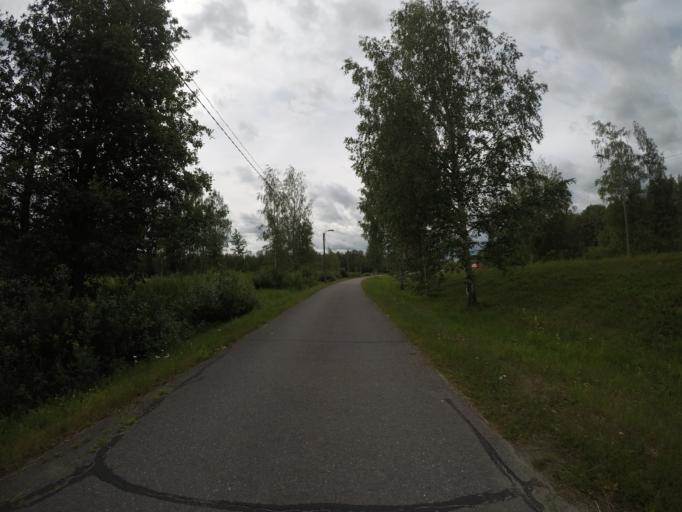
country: FI
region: Haeme
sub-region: Haemeenlinna
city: Haemeenlinna
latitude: 60.9779
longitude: 24.4981
